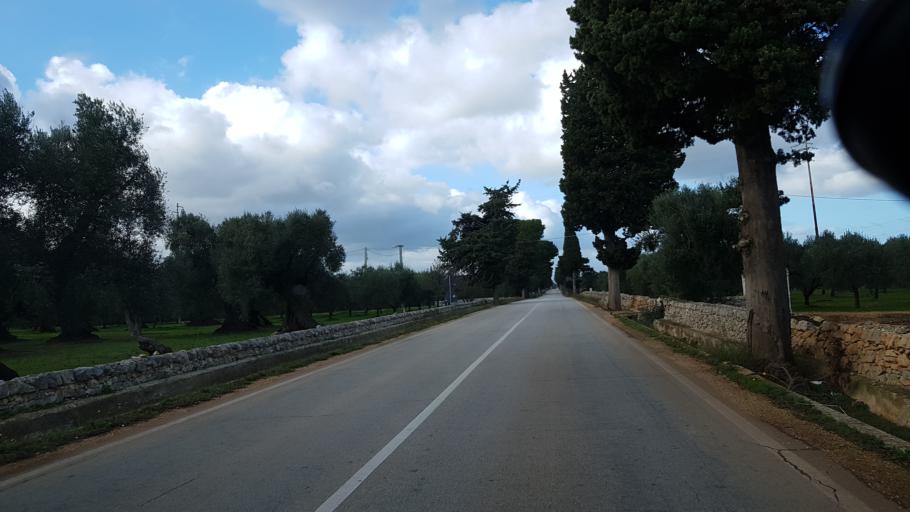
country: IT
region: Apulia
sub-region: Provincia di Brindisi
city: Montalbano
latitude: 40.7683
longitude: 17.5117
